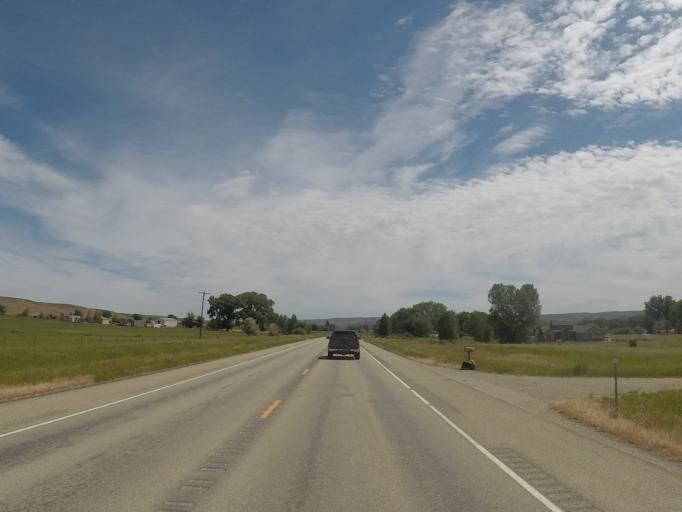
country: US
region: Montana
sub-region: Yellowstone County
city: Laurel
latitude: 45.5076
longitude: -108.9082
